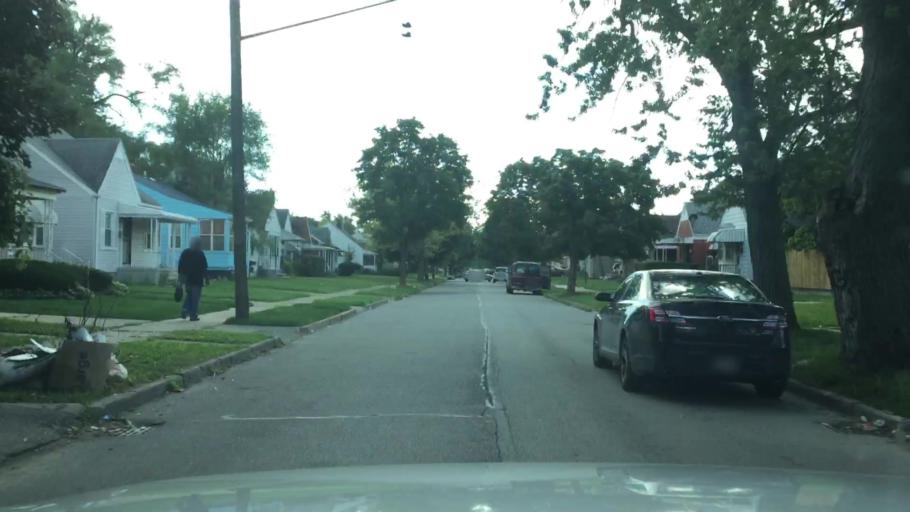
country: US
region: Michigan
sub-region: Wayne County
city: Dearborn Heights
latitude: 42.3416
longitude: -83.2242
